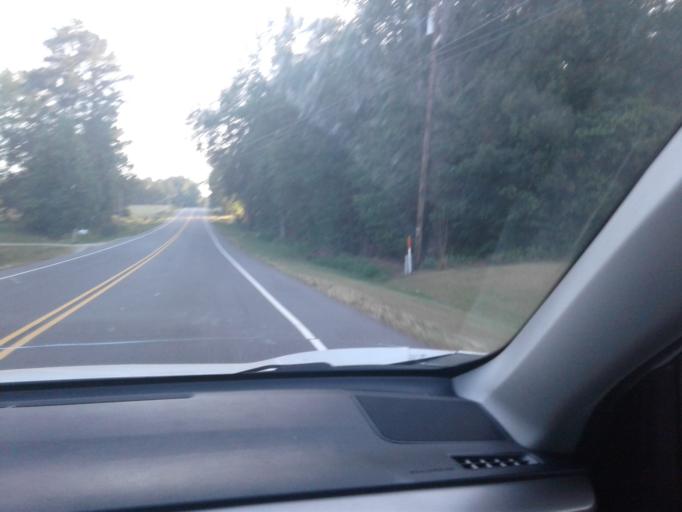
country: US
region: North Carolina
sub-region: Harnett County
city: Angier
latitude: 35.5008
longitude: -78.8134
